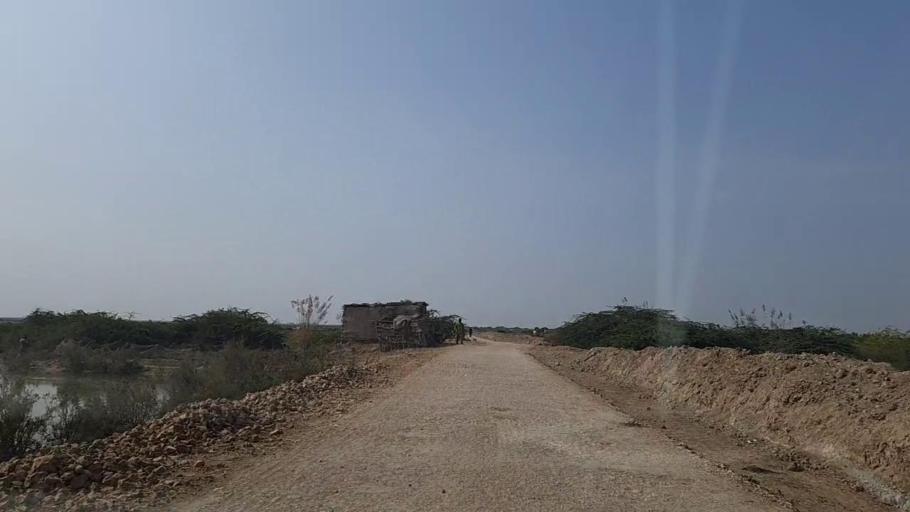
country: PK
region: Sindh
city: Chuhar Jamali
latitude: 24.1984
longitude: 67.8347
